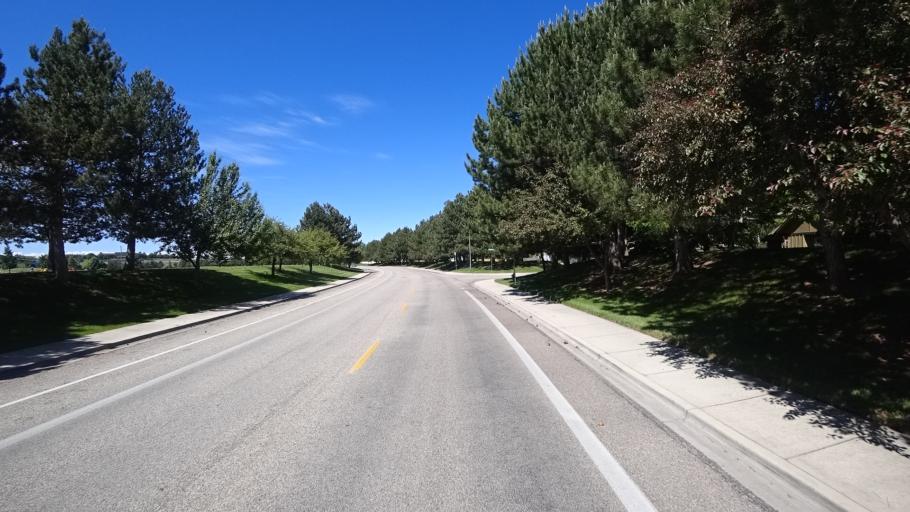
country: US
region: Idaho
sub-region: Ada County
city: Boise
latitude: 43.5512
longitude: -116.1488
